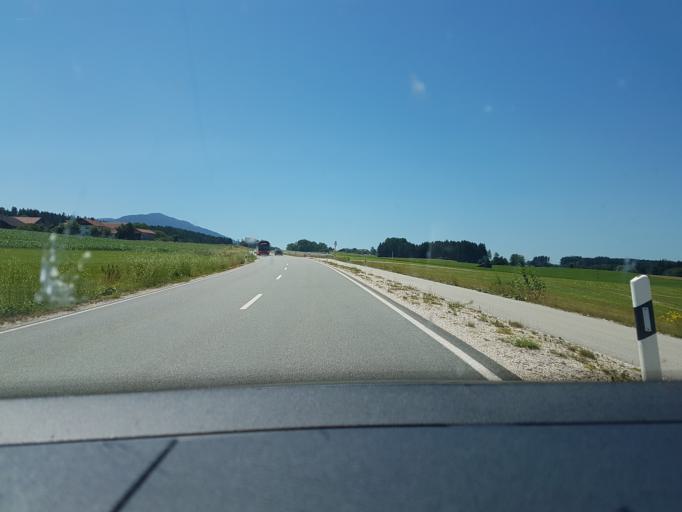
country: DE
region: Bavaria
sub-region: Upper Bavaria
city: Ainring
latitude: 47.8370
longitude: 12.9112
